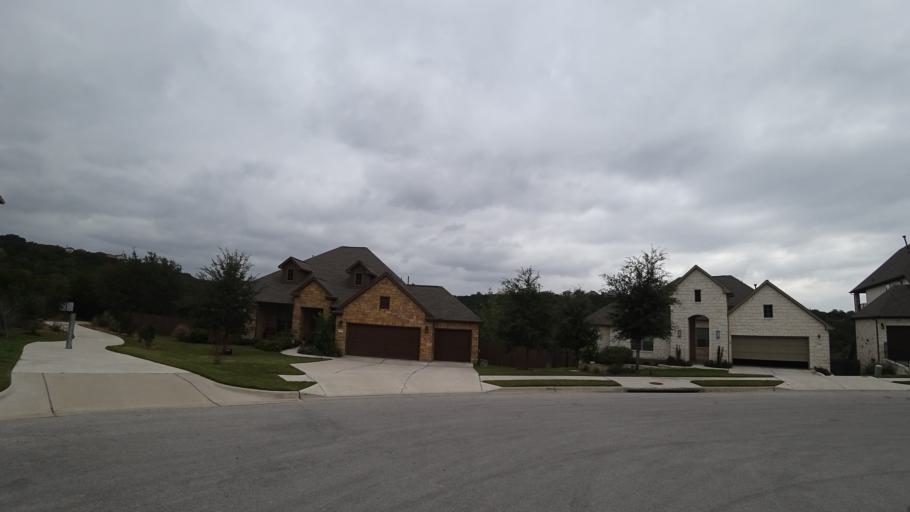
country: US
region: Texas
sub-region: Travis County
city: Bee Cave
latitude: 30.3454
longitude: -97.9063
